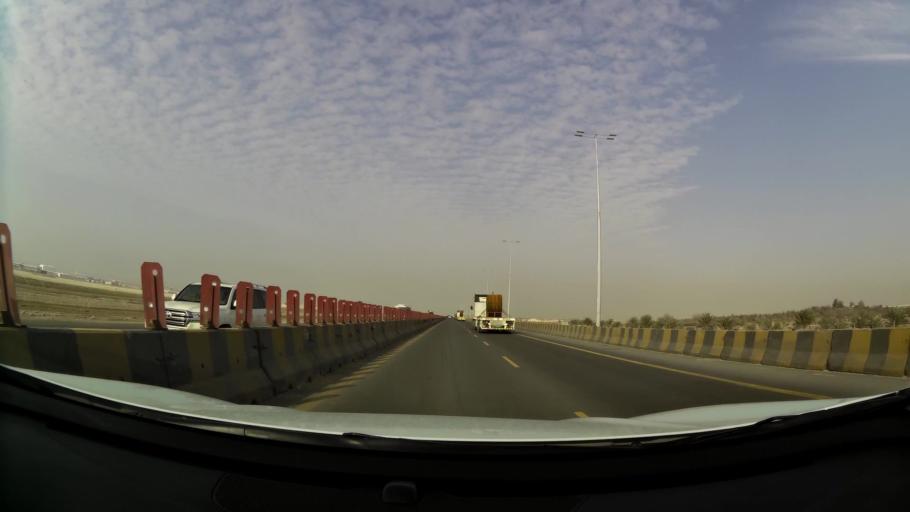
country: AE
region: Abu Dhabi
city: Abu Dhabi
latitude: 24.2608
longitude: 54.4881
